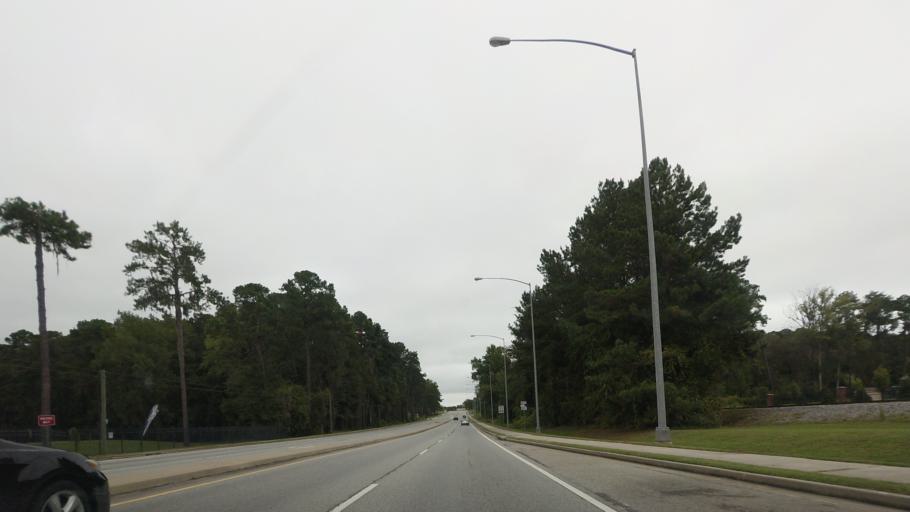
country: US
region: Georgia
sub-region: Berrien County
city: Ray City
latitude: 30.9798
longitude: -83.2089
